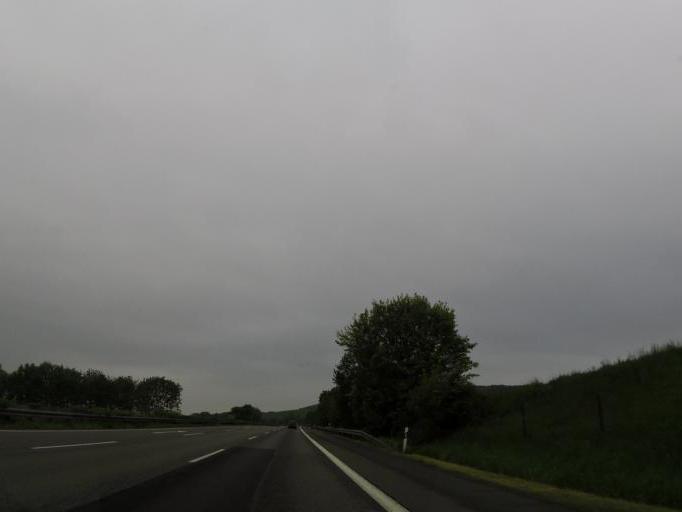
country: DE
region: Lower Saxony
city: Kalefeld
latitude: 51.7650
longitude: 10.0202
